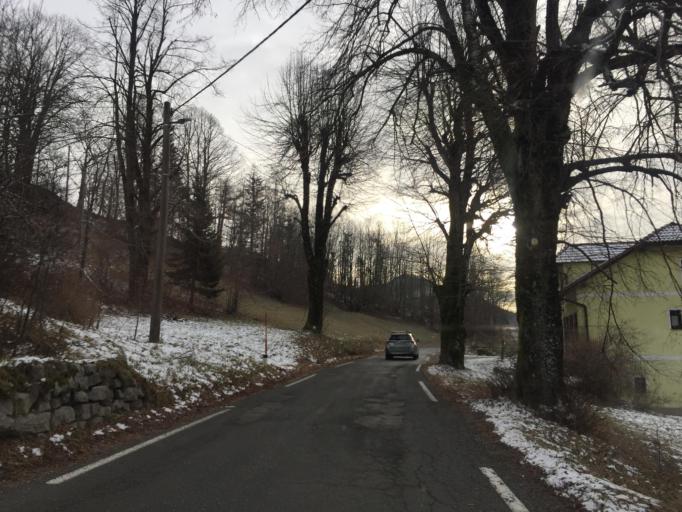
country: SI
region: Nova Gorica
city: Sempas
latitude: 46.0130
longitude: 13.7897
